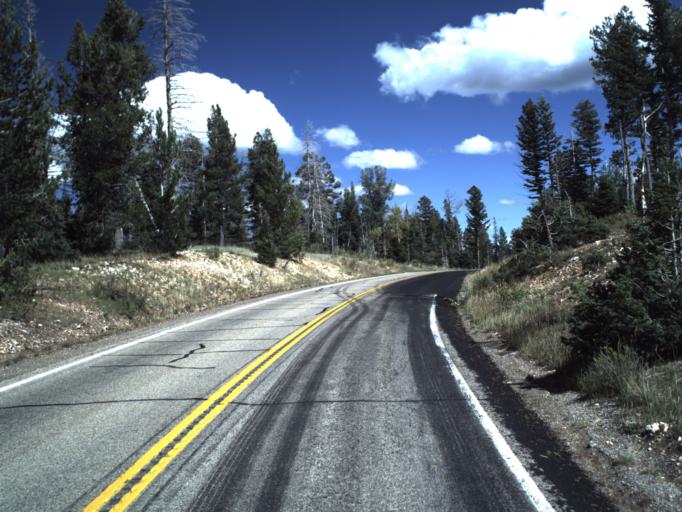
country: US
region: Utah
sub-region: Iron County
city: Parowan
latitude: 37.5279
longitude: -112.7567
